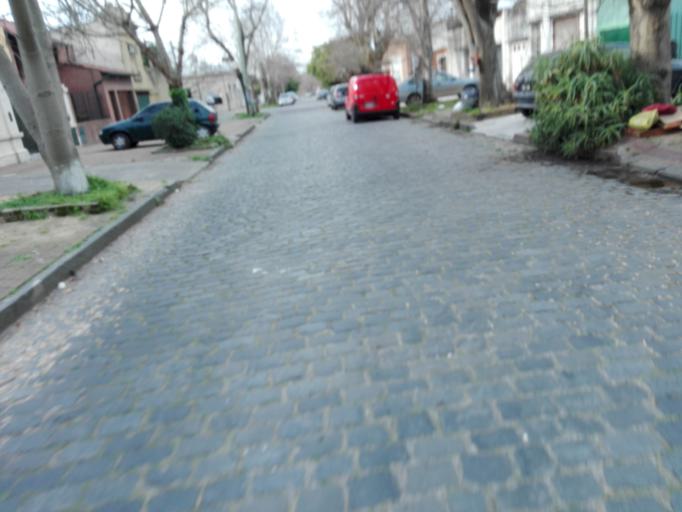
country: AR
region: Buenos Aires
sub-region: Partido de La Plata
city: La Plata
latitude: -34.8978
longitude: -57.9577
